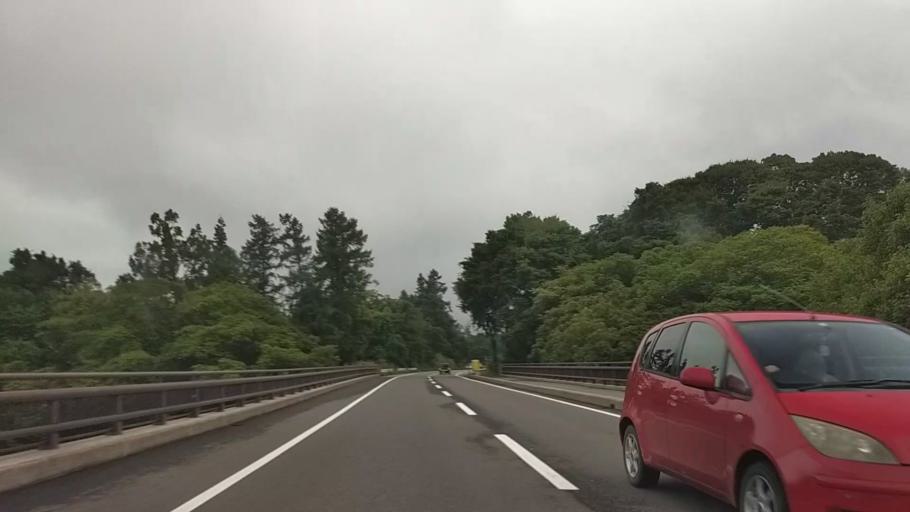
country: JP
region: Nagano
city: Iiyama
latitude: 36.8175
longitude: 138.3444
